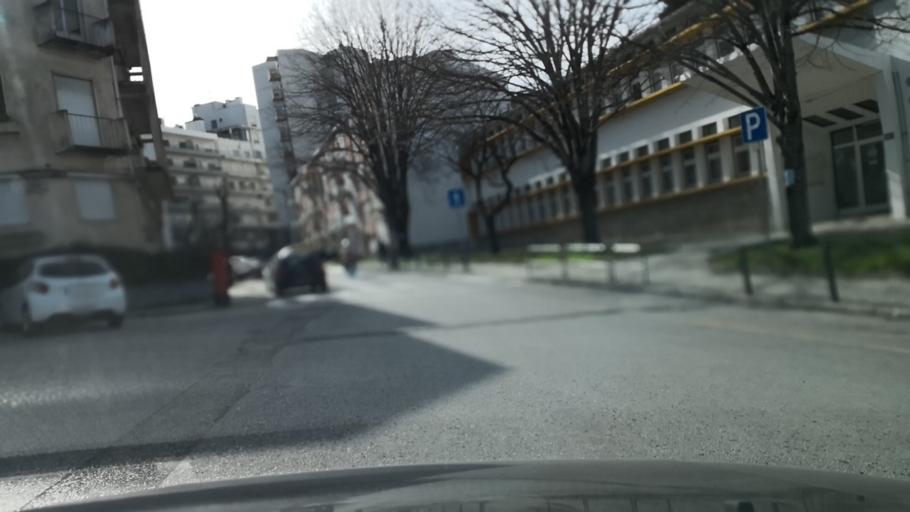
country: PT
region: Leiria
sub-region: Leiria
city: Leiria
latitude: 39.7417
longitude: -8.8052
